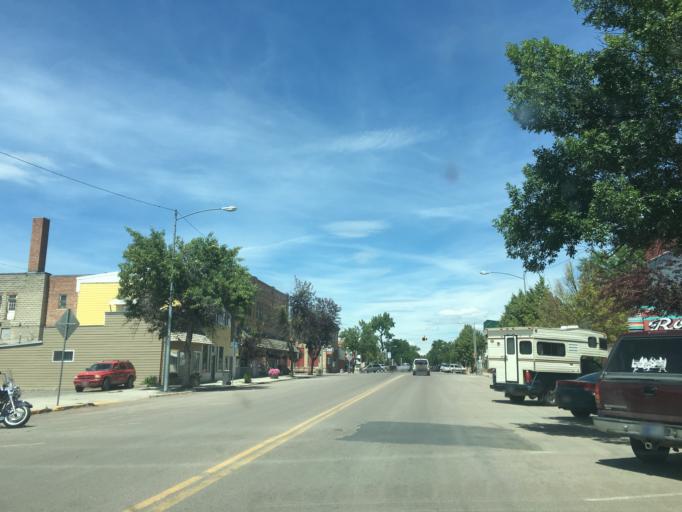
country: US
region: Montana
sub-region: Teton County
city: Choteau
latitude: 47.8115
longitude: -112.1829
